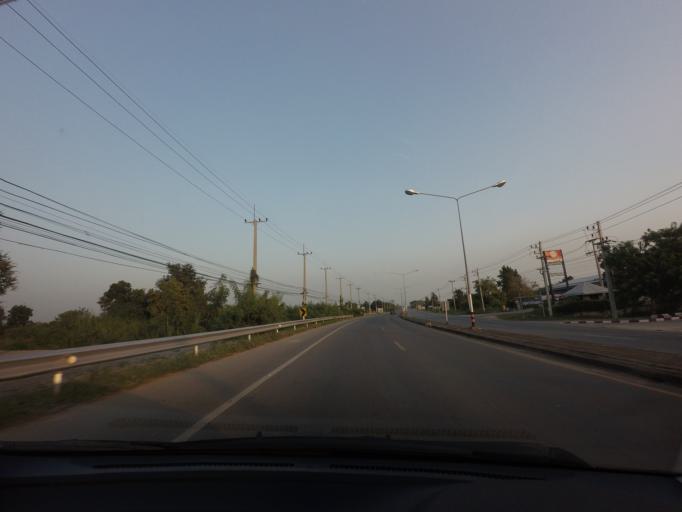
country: TH
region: Sukhothai
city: Sukhothai
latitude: 17.0261
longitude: 99.8877
